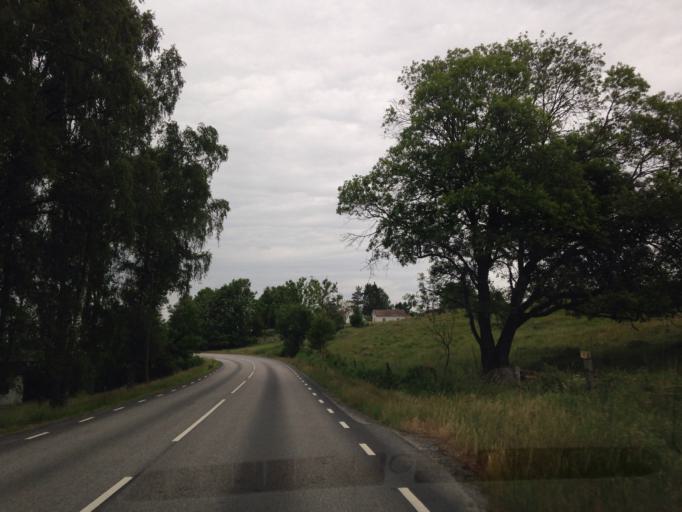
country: SE
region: Vaestra Goetaland
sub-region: Marks Kommun
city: Horred
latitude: 57.4835
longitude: 12.5216
